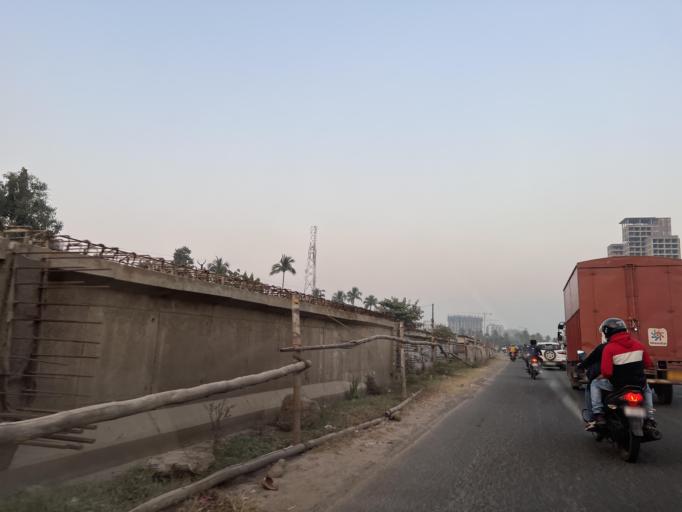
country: IN
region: Odisha
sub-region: Khordha
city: Bhubaneshwar
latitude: 20.3187
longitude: 85.8802
